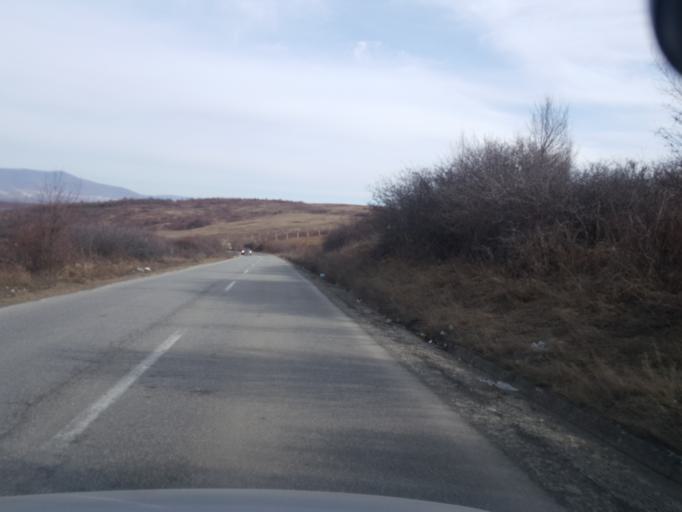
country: XK
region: Gjakova
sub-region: Komuna e Gjakoves
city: Gjakove
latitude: 42.4315
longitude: 20.4507
